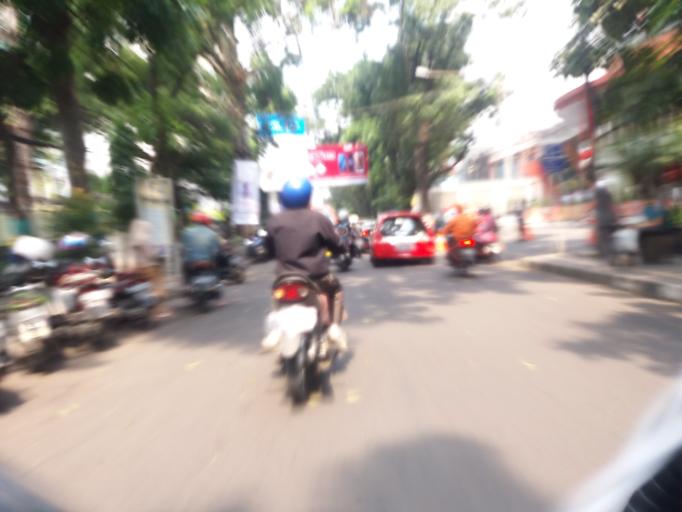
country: ID
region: West Java
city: Bandung
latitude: -6.9077
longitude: 107.6093
